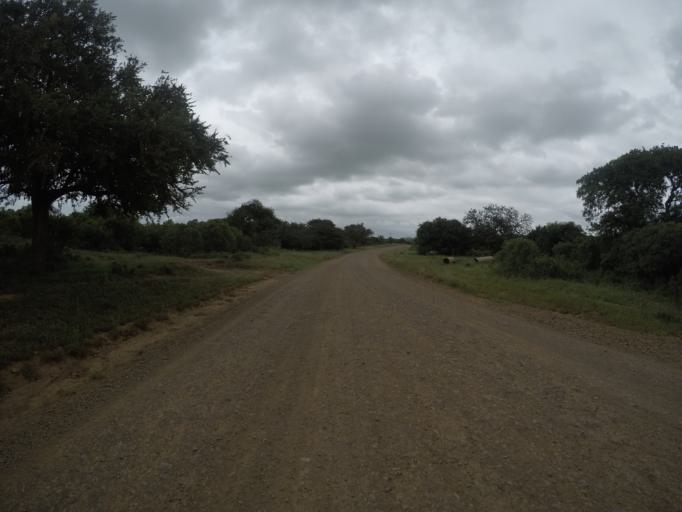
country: ZA
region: KwaZulu-Natal
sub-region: uThungulu District Municipality
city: Empangeni
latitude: -28.5937
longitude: 31.8358
